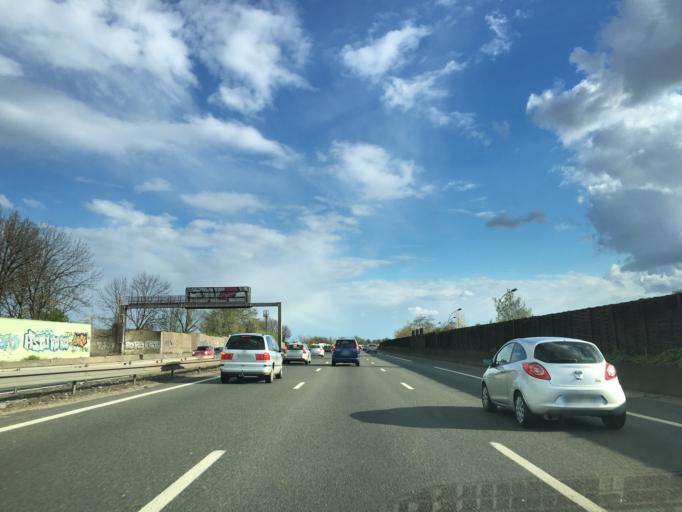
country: FR
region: Ile-de-France
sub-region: Departement de Seine-Saint-Denis
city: Aulnay-sous-Bois
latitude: 48.9411
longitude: 2.4787
